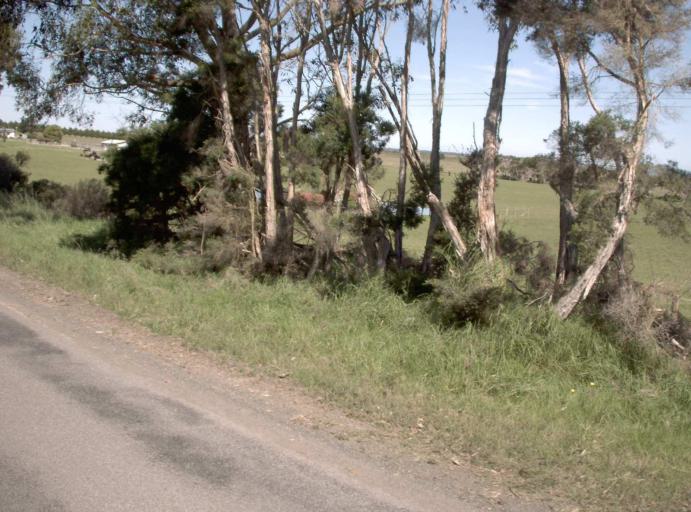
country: AU
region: Victoria
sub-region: Latrobe
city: Morwell
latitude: -38.6668
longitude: 146.3407
